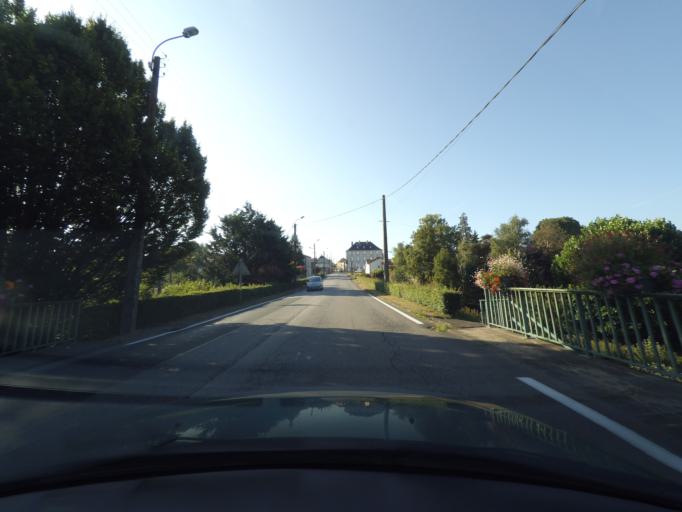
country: FR
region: Poitou-Charentes
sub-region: Departement des Deux-Sevres
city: Chiche
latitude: 46.7990
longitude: -0.3616
